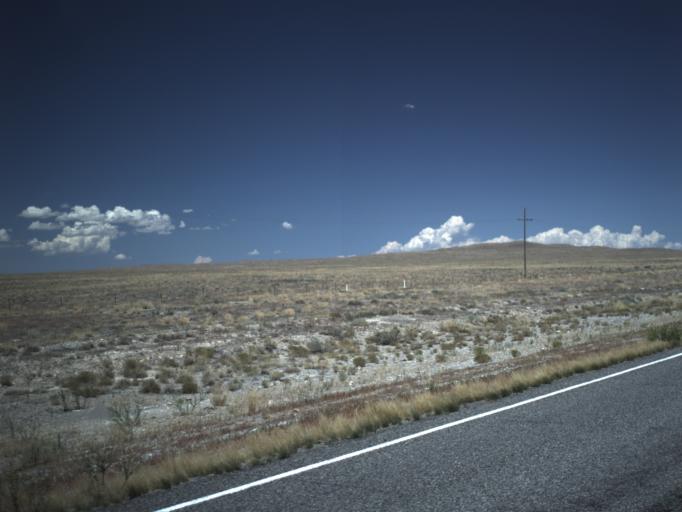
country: US
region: Utah
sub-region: Millard County
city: Delta
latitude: 39.1342
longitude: -113.0966
